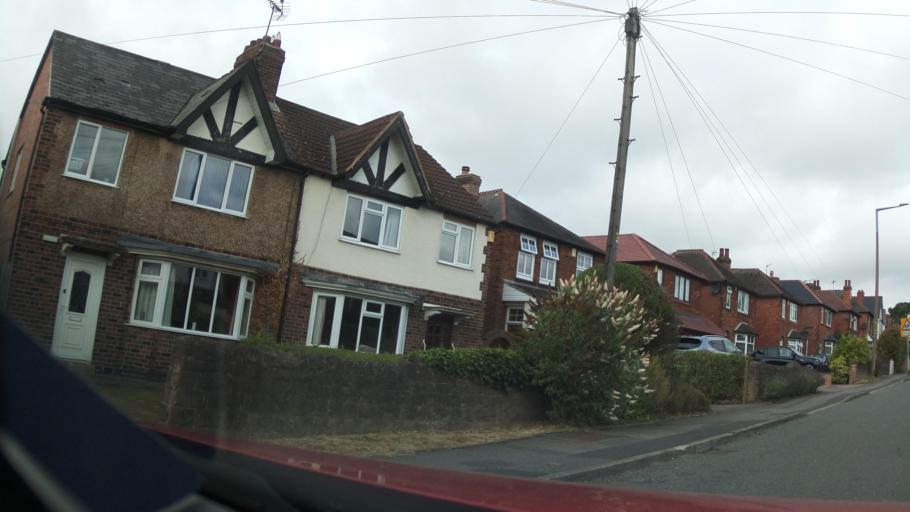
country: GB
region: England
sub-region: Derbyshire
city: Long Eaton
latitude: 52.9203
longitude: -1.3054
